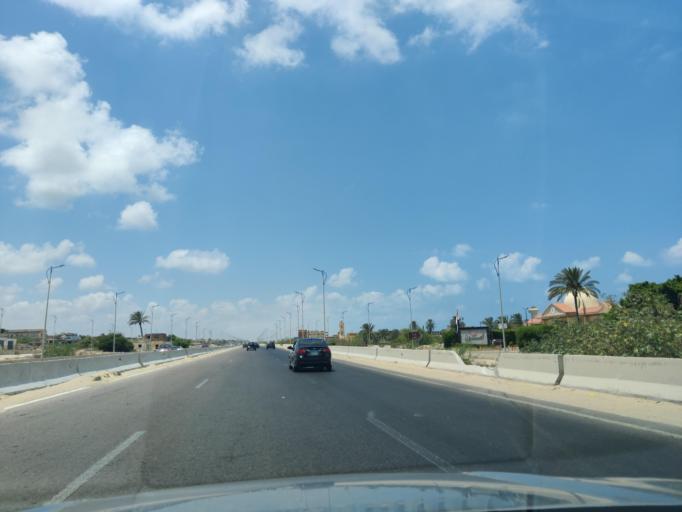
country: EG
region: Alexandria
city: Alexandria
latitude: 30.9994
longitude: 29.6093
